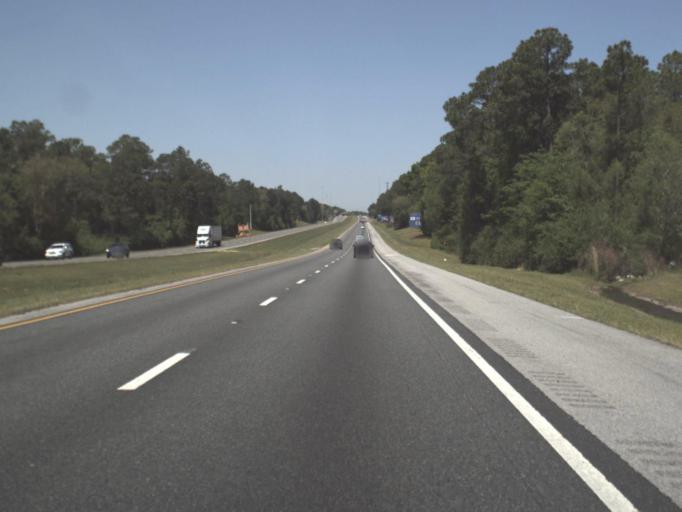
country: US
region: Florida
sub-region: Escambia County
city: Ensley
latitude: 30.5148
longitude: -87.3008
